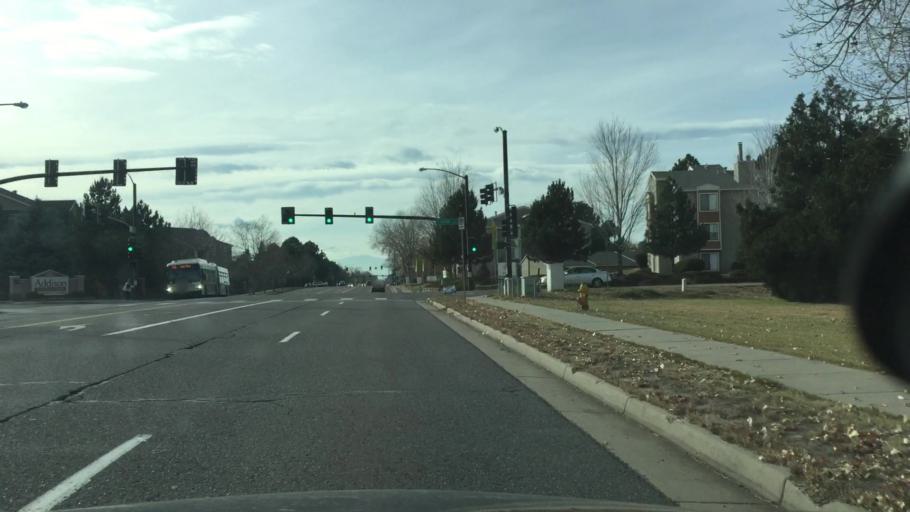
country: US
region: Colorado
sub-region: Arapahoe County
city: Glendale
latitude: 39.6894
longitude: -104.8817
